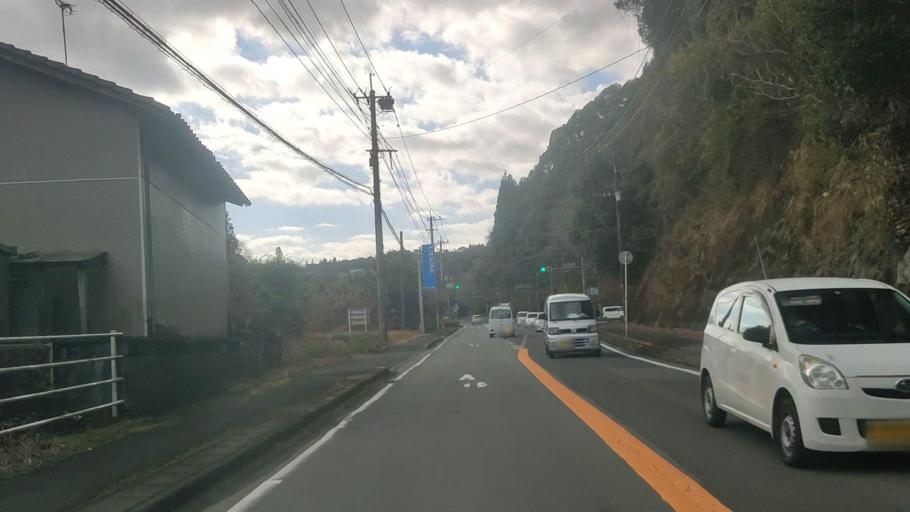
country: JP
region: Kagoshima
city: Kajiki
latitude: 31.8953
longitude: 130.6947
